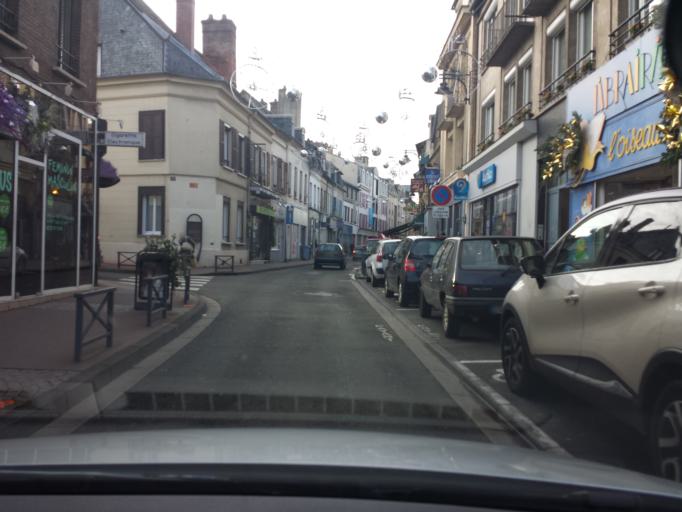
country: FR
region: Haute-Normandie
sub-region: Departement de l'Eure
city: Evreux
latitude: 49.0254
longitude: 1.1460
